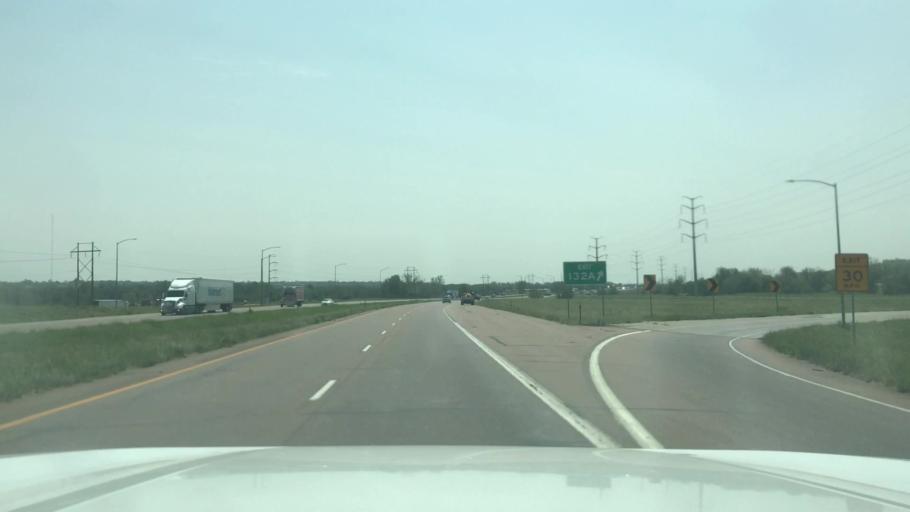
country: US
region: Colorado
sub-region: El Paso County
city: Security-Widefield
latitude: 38.7242
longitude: -104.7325
